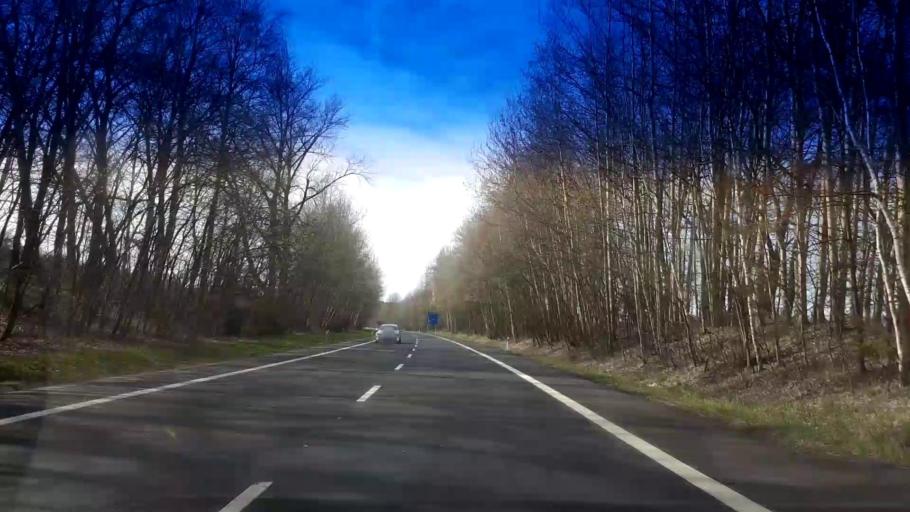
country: CZ
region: Karlovarsky
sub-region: Okres Cheb
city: Frantiskovy Lazne
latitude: 50.0979
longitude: 12.3286
